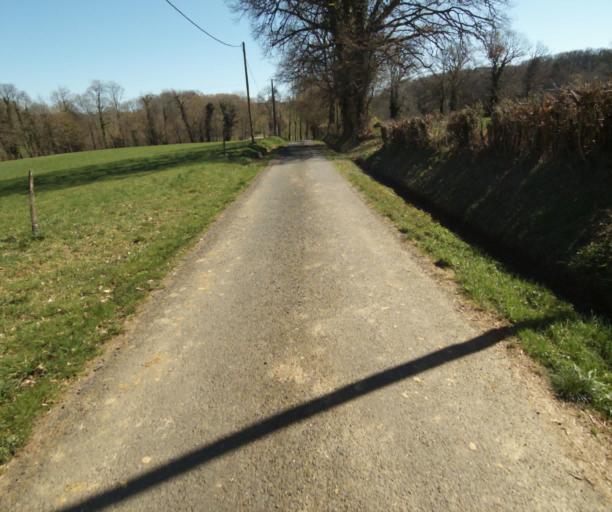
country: FR
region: Limousin
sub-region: Departement de la Correze
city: Saint-Clement
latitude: 45.3940
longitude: 1.6448
